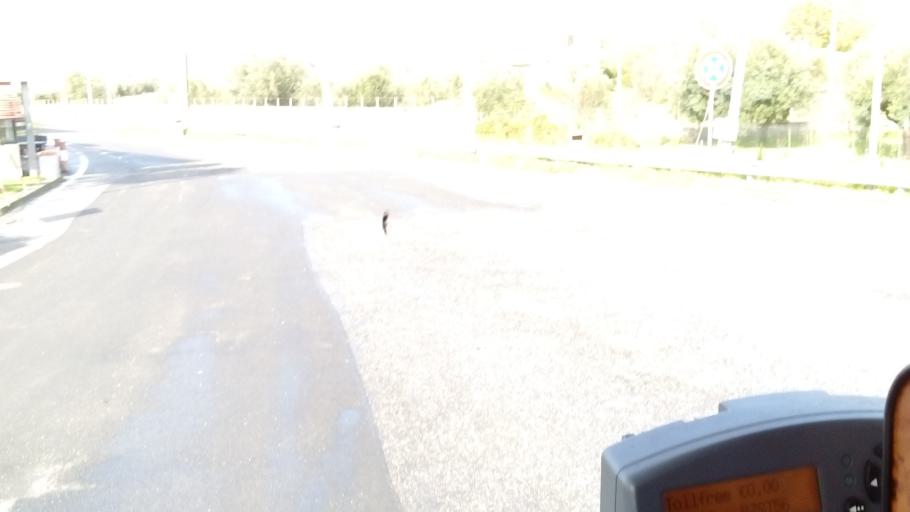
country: IT
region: Calabria
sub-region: Provincia di Catanzaro
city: Santa Eufemia Lamezia
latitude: 38.9301
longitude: 16.2375
